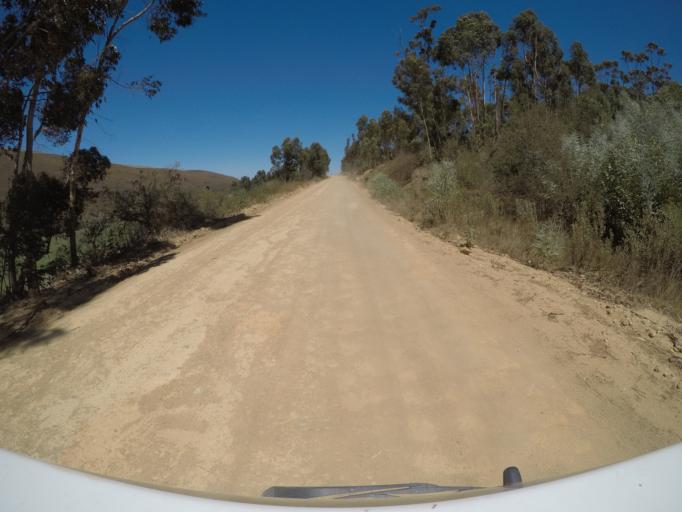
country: ZA
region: Western Cape
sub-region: Overberg District Municipality
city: Grabouw
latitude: -34.2107
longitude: 19.2123
